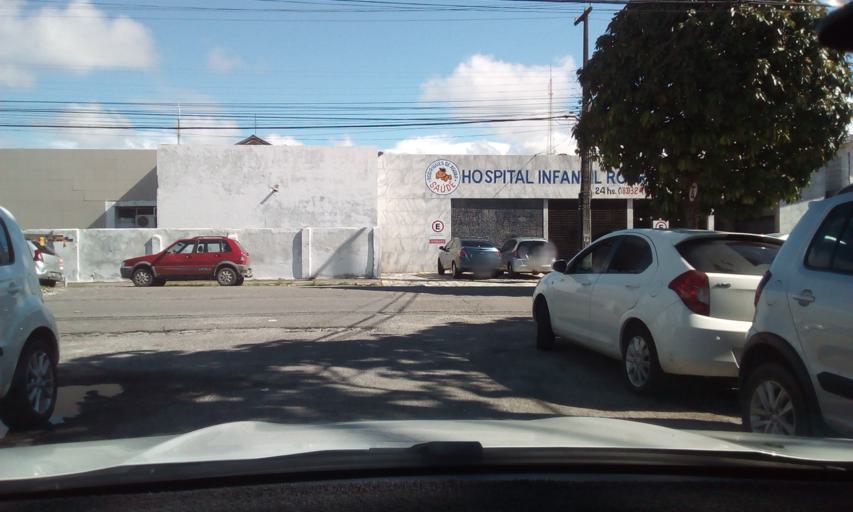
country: BR
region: Paraiba
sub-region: Joao Pessoa
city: Joao Pessoa
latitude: -7.1195
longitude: -34.8750
